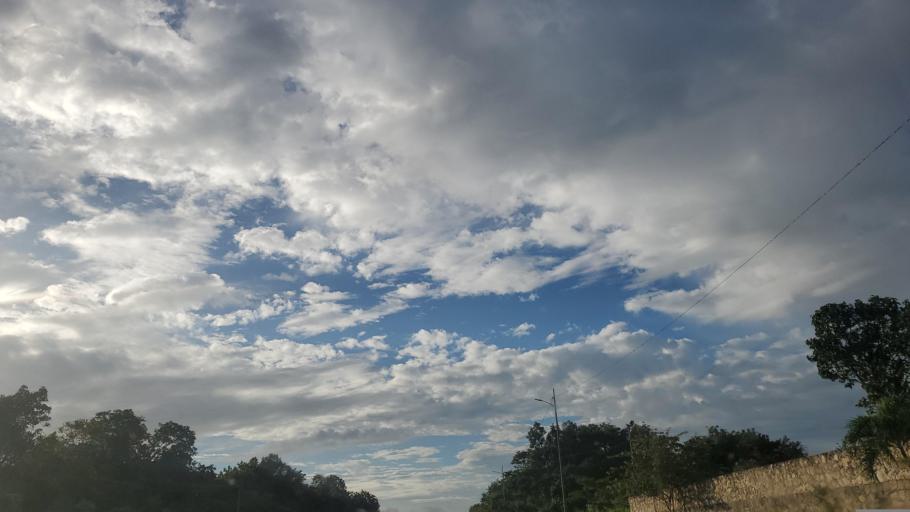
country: MX
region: Quintana Roo
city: Tulum
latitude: 20.2085
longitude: -87.4841
